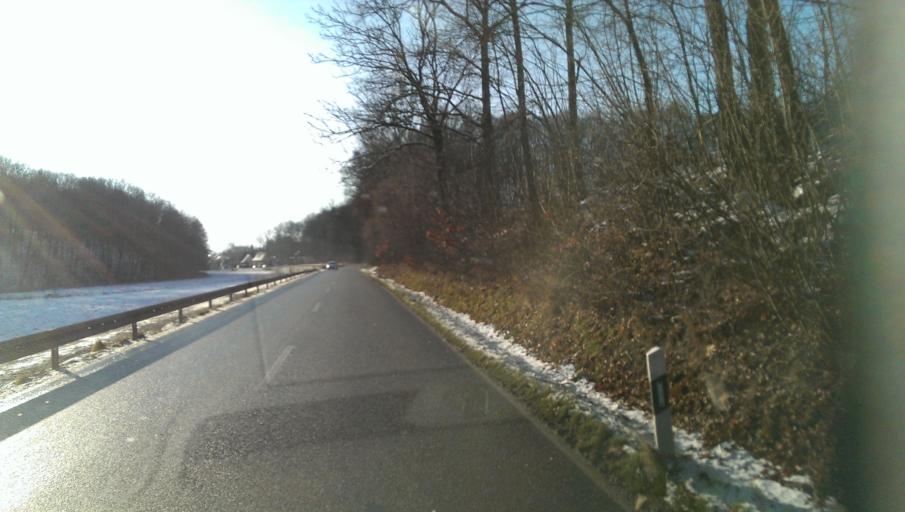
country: DE
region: Saxony
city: Dippoldiswalde
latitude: 50.8935
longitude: 13.6505
